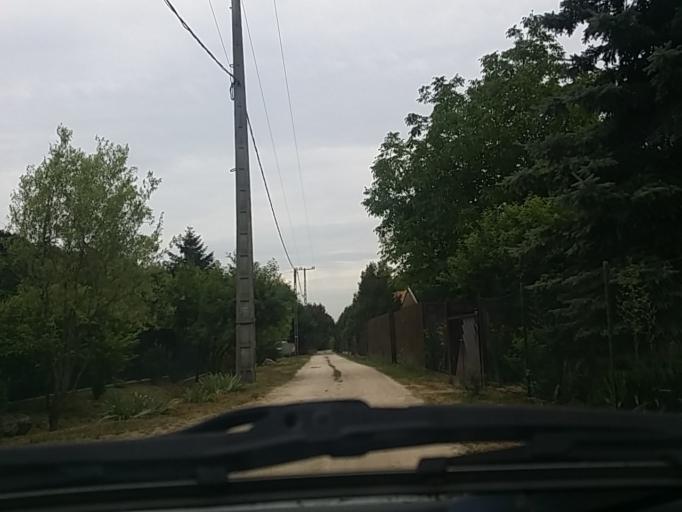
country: HU
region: Pest
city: Solymar
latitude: 47.6107
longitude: 18.9548
